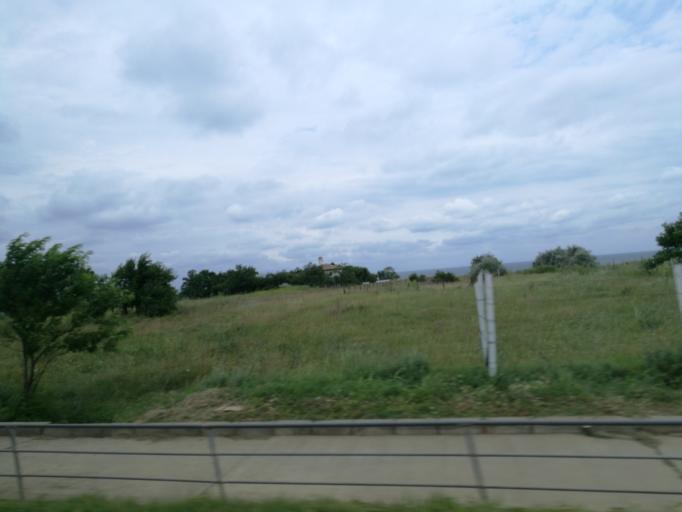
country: RO
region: Constanta
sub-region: Municipiul Mangalia
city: Mangalia
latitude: 43.7729
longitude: 28.5767
